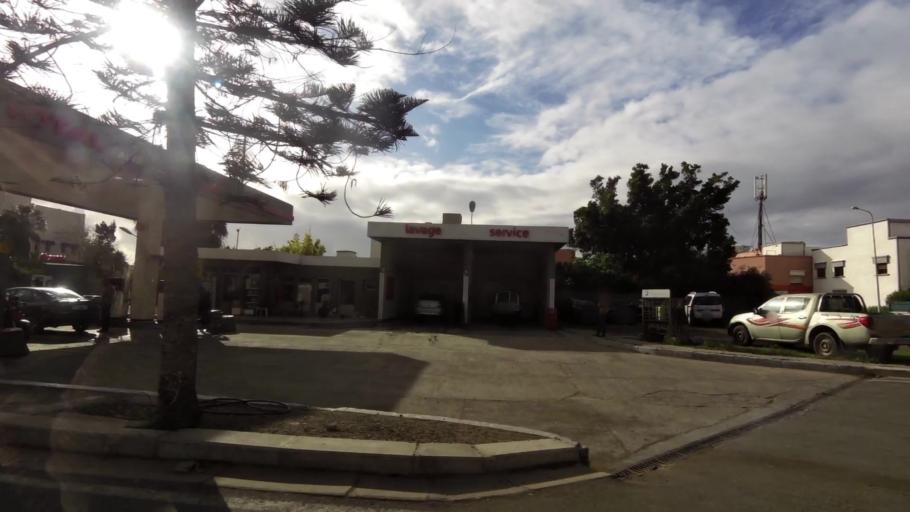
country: MA
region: Doukkala-Abda
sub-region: El-Jadida
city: El Jadida
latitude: 33.2469
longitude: -8.5187
